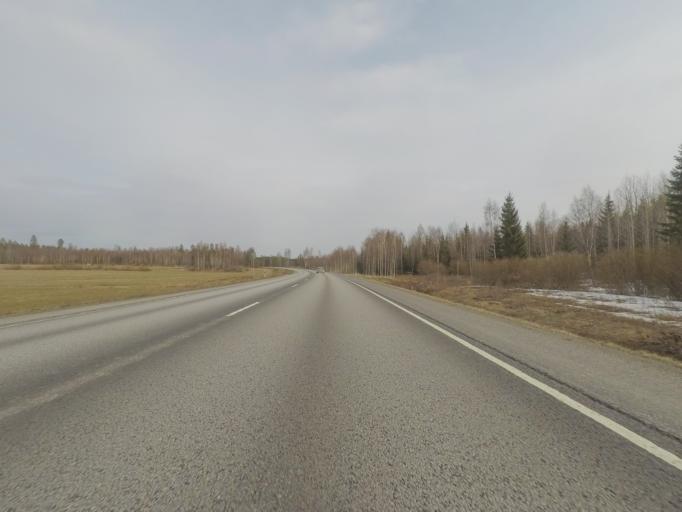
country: FI
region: Central Finland
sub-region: Jyvaeskylae
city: Hankasalmi
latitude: 62.2530
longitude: 26.2505
